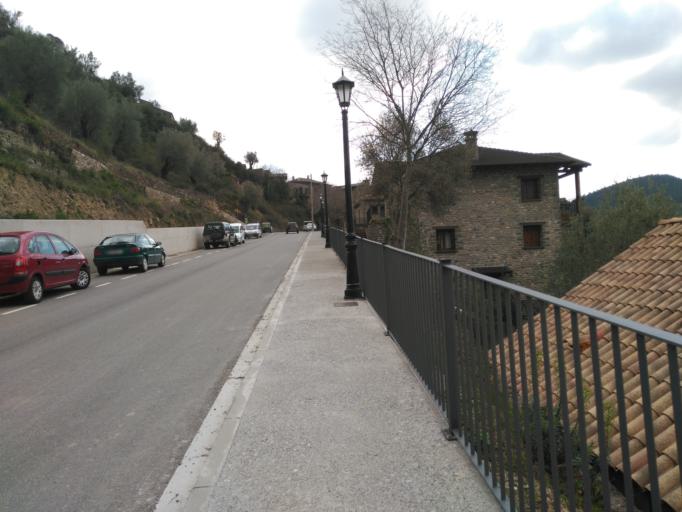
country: ES
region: Aragon
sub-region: Provincia de Huesca
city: Boltana
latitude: 42.4483
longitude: 0.0665
